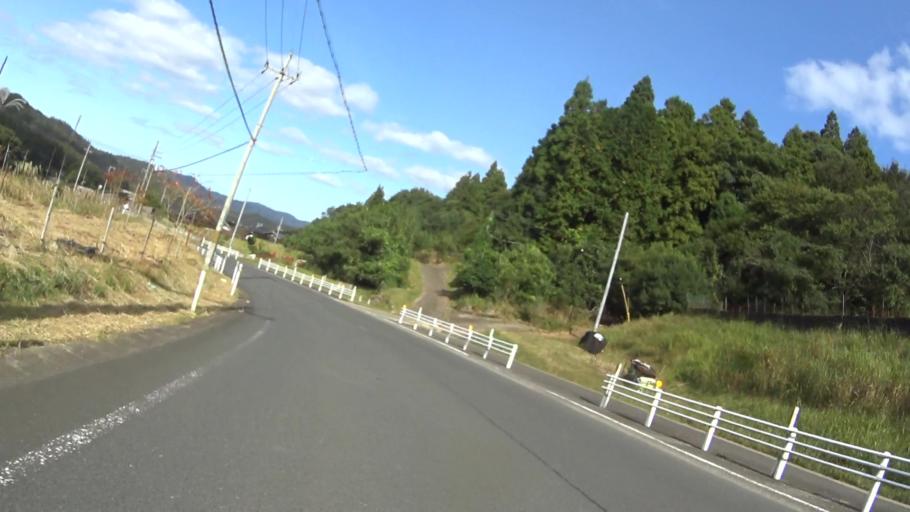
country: JP
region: Hyogo
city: Toyooka
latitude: 35.5421
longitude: 134.9780
